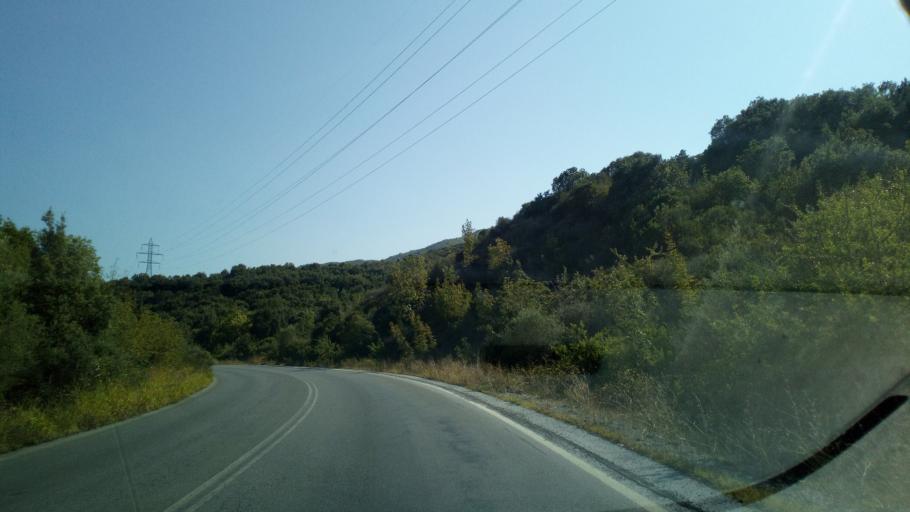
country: GR
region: Central Macedonia
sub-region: Nomos Thessalonikis
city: Stavros
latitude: 40.6427
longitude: 23.7476
